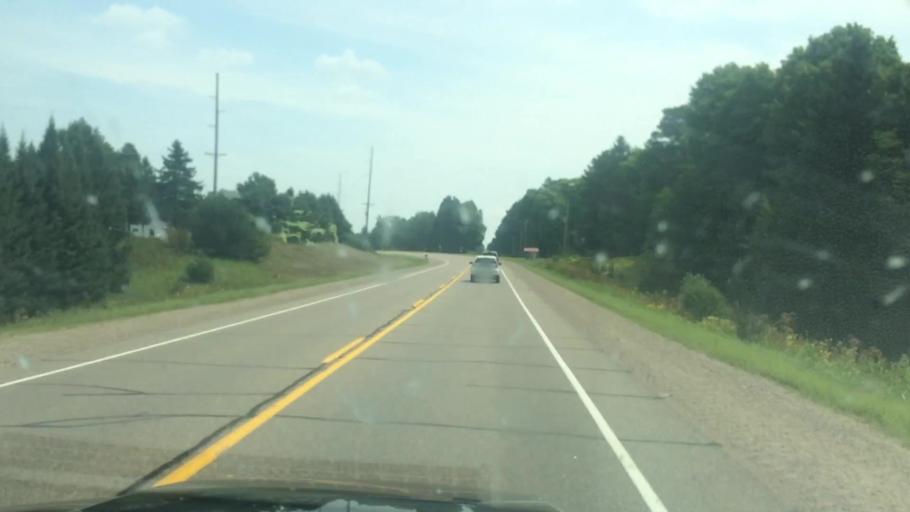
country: US
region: Wisconsin
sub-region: Langlade County
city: Antigo
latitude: 45.1612
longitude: -89.0214
